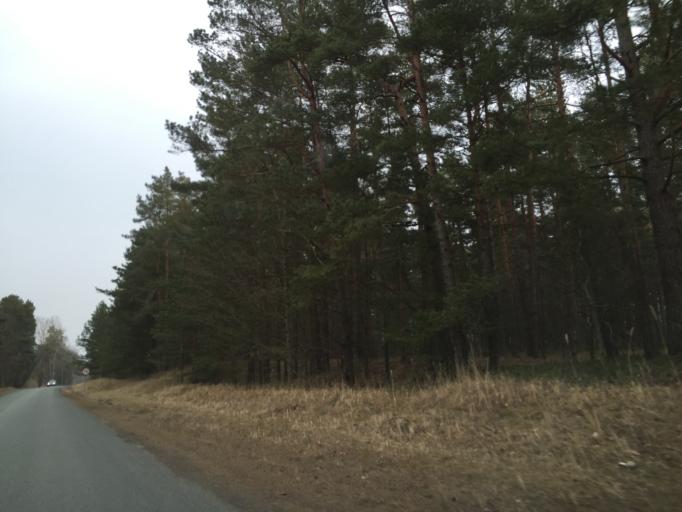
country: LV
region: Salacgrivas
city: Ainazi
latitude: 57.9940
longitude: 24.4289
